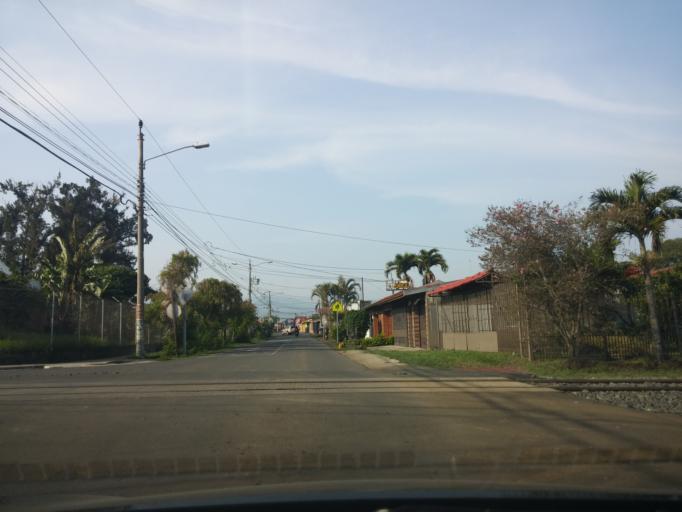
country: CR
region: Heredia
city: Llorente
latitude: 10.0038
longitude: -84.1557
